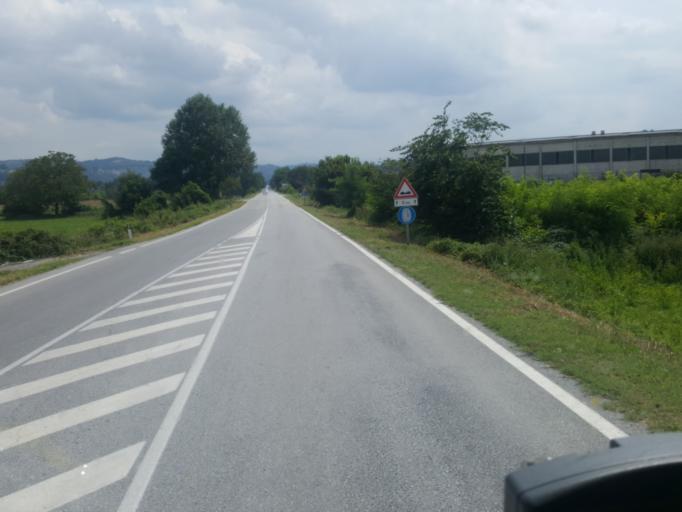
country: IT
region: Piedmont
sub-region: Provincia di Cuneo
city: Piozzo
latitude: 44.5219
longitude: 7.9002
